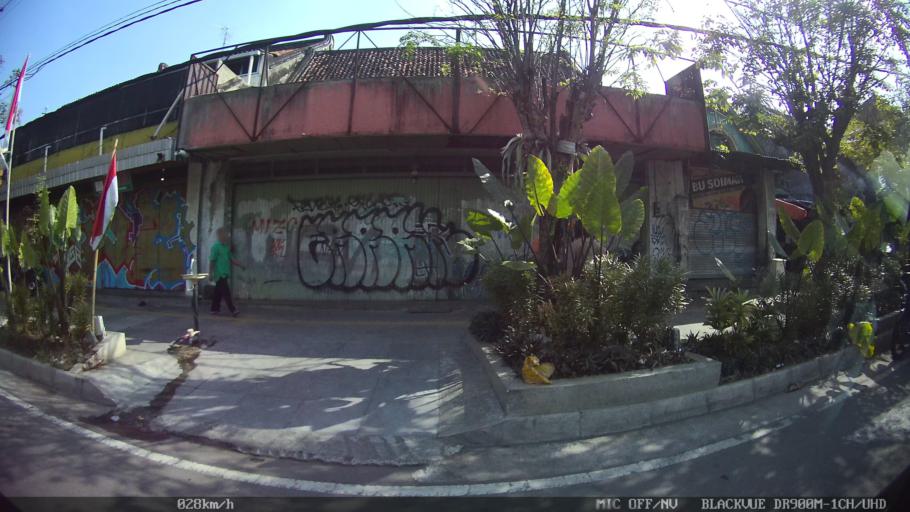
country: ID
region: Daerah Istimewa Yogyakarta
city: Yogyakarta
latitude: -7.8011
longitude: 110.3582
